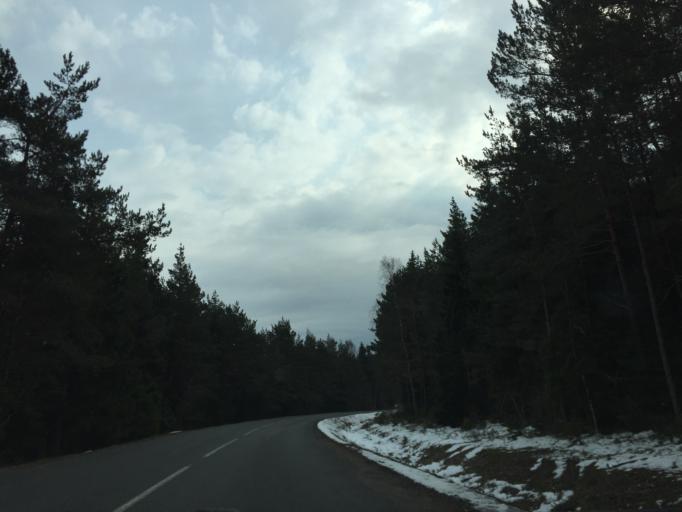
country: EE
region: Saare
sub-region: Kuressaare linn
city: Kuressaare
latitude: 58.4508
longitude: 22.0521
